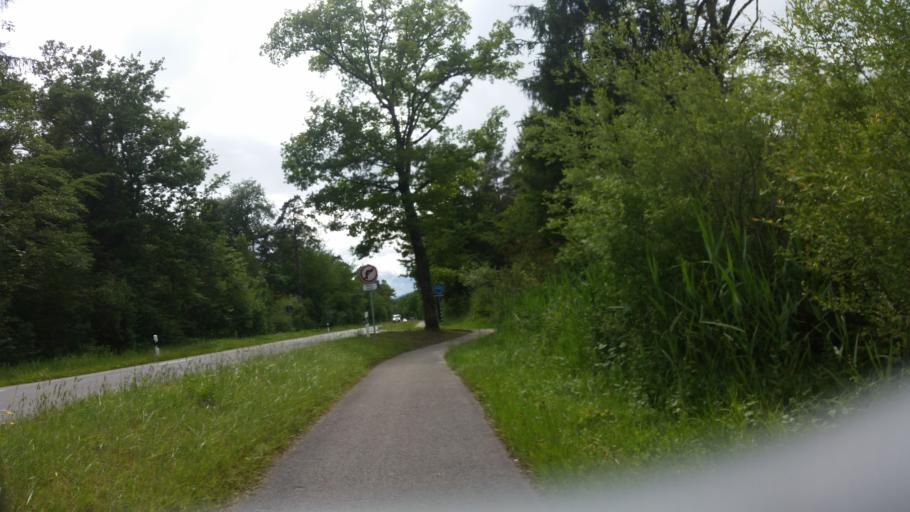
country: CH
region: Vaud
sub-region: Jura-Nord vaudois District
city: Yvonand
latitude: 46.7997
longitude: 6.7081
